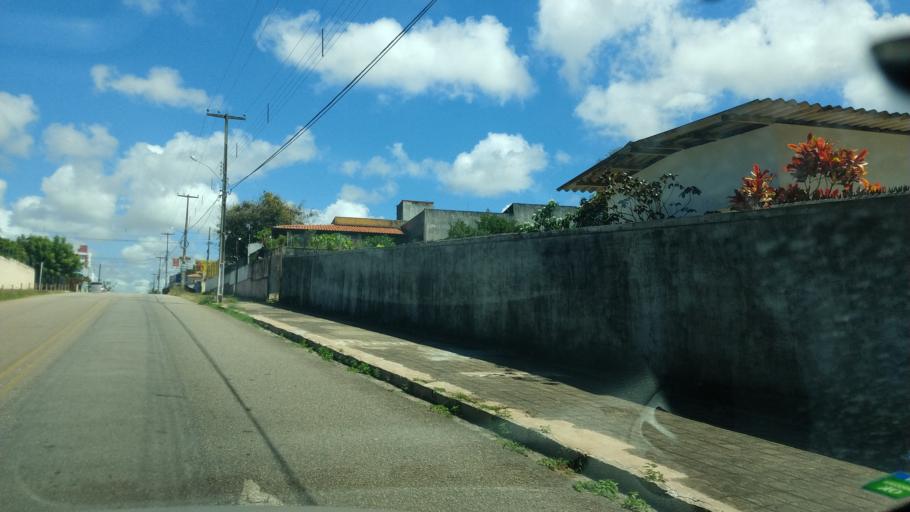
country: BR
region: Rio Grande do Norte
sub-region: Natal
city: Natal
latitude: -5.8492
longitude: -35.2001
